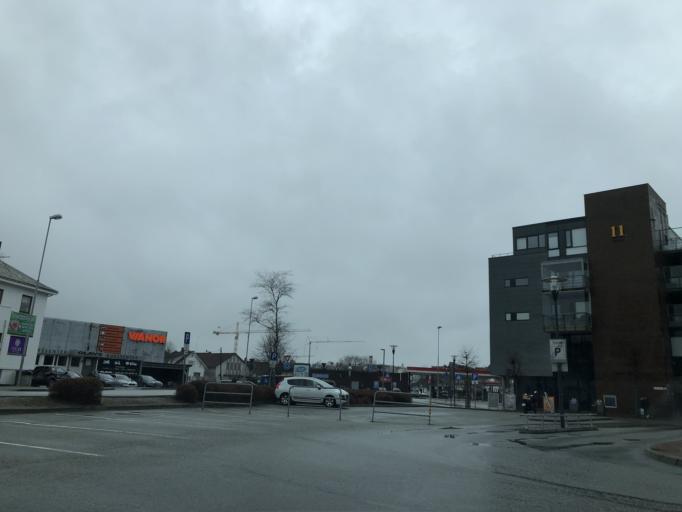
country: NO
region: Rogaland
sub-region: Sandnes
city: Sandnes
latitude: 58.8489
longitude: 5.7388
